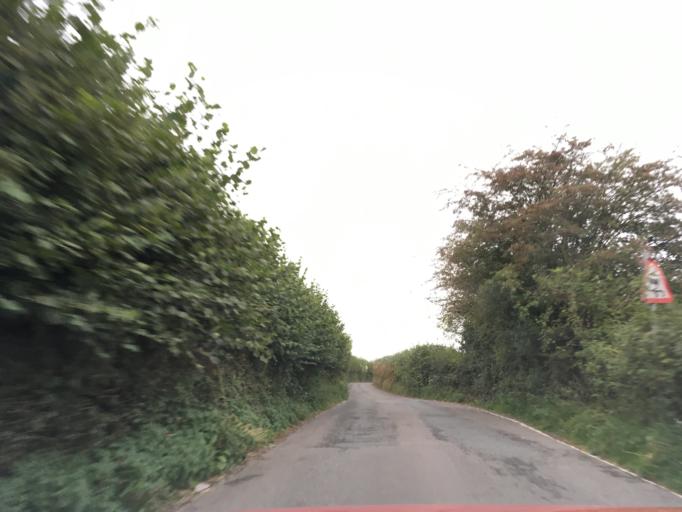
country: GB
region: Wales
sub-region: Newport
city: Langstone
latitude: 51.6181
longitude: -2.9077
